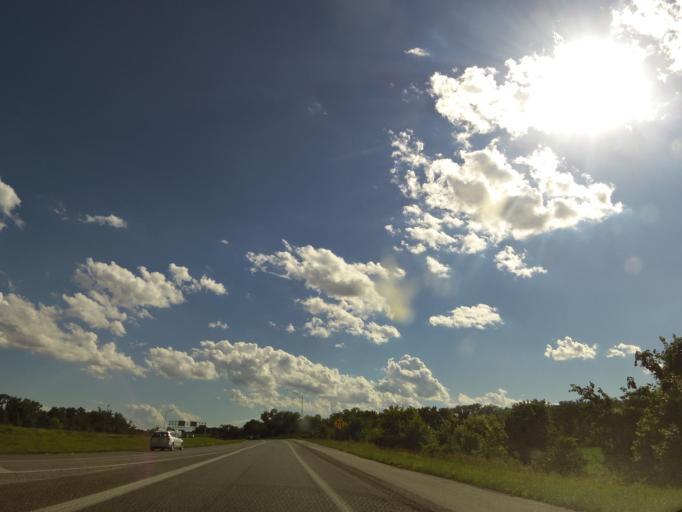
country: US
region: Illinois
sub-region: Adams County
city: Quincy
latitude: 39.9343
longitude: -91.5191
